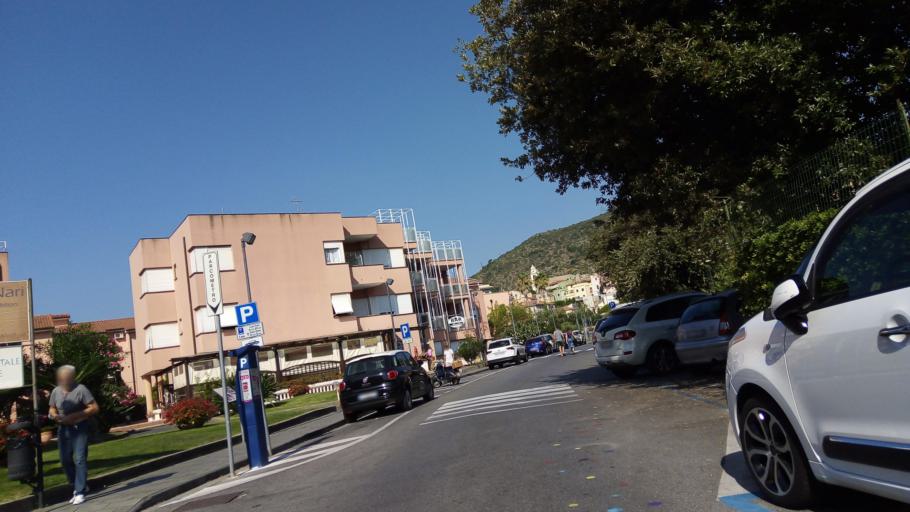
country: IT
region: Liguria
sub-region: Provincia di Savona
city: Borgio
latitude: 44.1592
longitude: 8.3080
